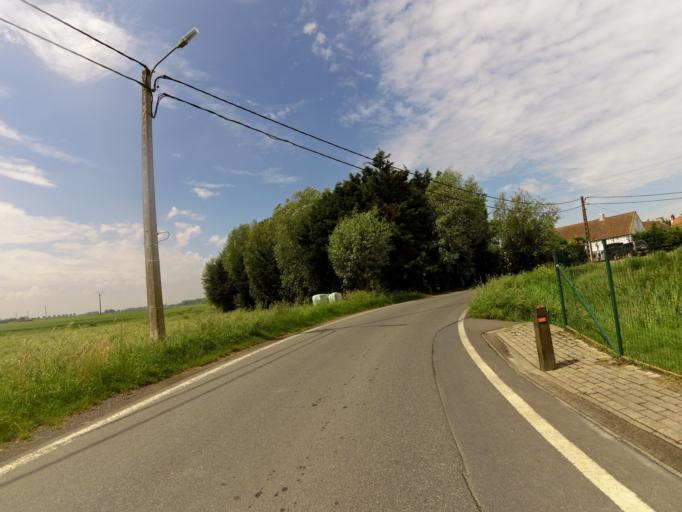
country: BE
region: Flanders
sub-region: Provincie West-Vlaanderen
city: Middelkerke
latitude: 51.1492
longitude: 2.8019
